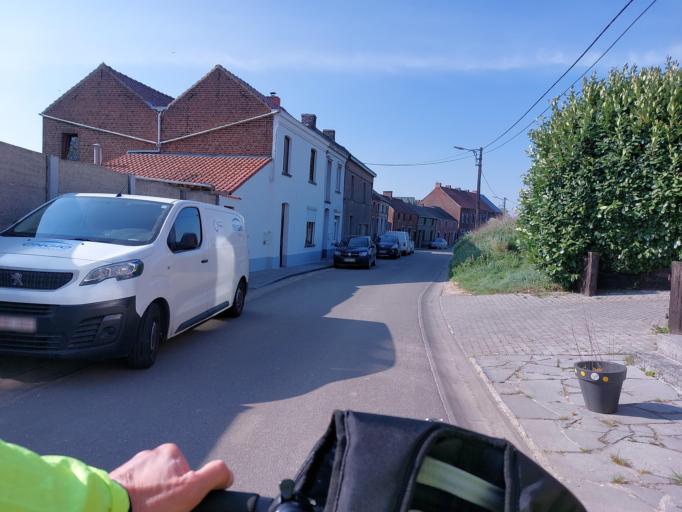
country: BE
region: Wallonia
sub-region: Province du Hainaut
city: Ecaussinnes-d'Enghien
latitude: 50.5562
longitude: 4.1603
